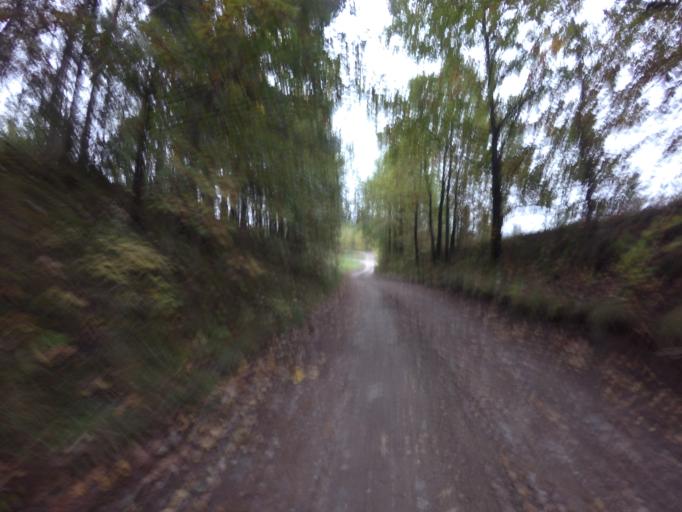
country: PL
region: Pomeranian Voivodeship
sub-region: Powiat kartuski
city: Stezyca
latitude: 54.1708
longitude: 17.9592
